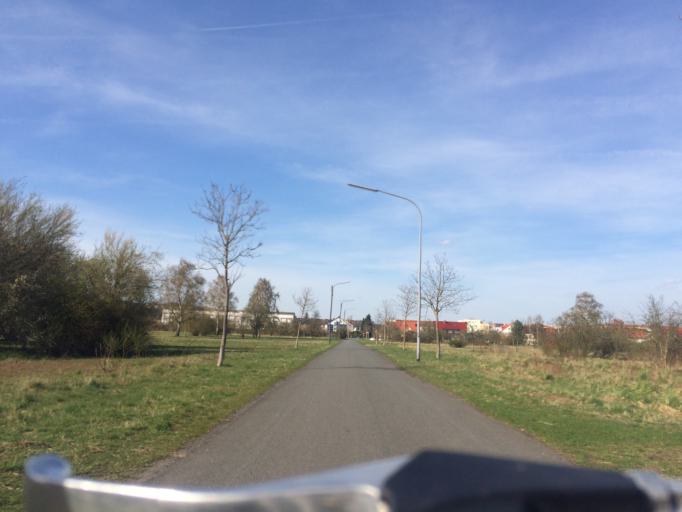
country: DE
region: Hesse
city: Morfelden-Walldorf
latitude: 49.9926
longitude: 8.5679
